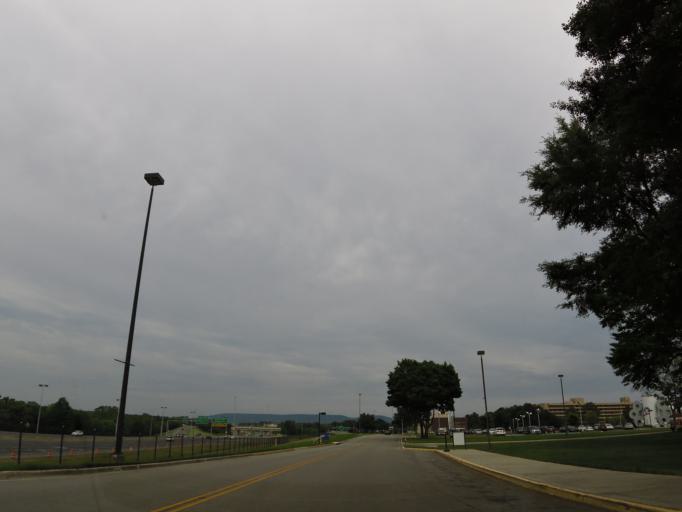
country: US
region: Alabama
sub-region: Madison County
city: Redstone Arsenal
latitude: 34.7124
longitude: -86.6540
